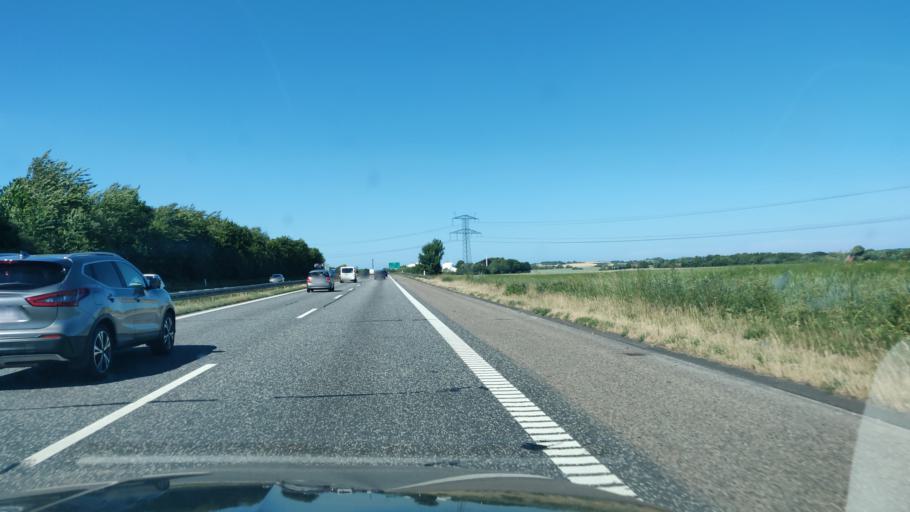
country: DK
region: Central Jutland
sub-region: Arhus Kommune
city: Trige
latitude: 56.2771
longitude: 10.1346
